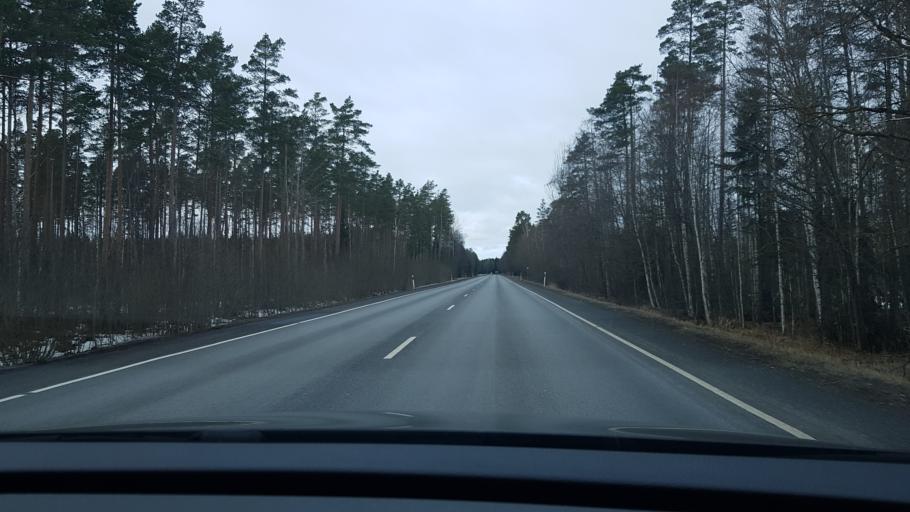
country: EE
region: Paernumaa
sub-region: Paikuse vald
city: Paikuse
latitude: 58.2434
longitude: 24.6902
